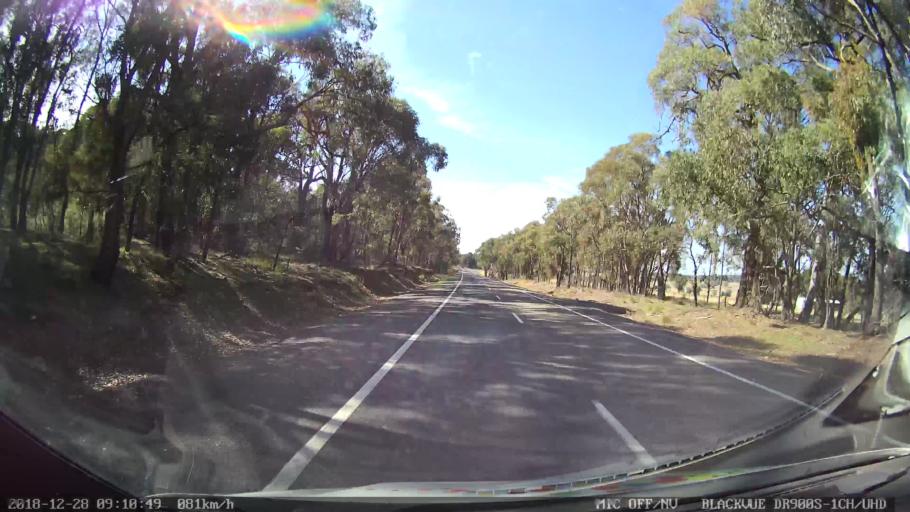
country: AU
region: New South Wales
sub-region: Upper Lachlan Shire
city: Crookwell
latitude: -34.2363
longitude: 149.3373
